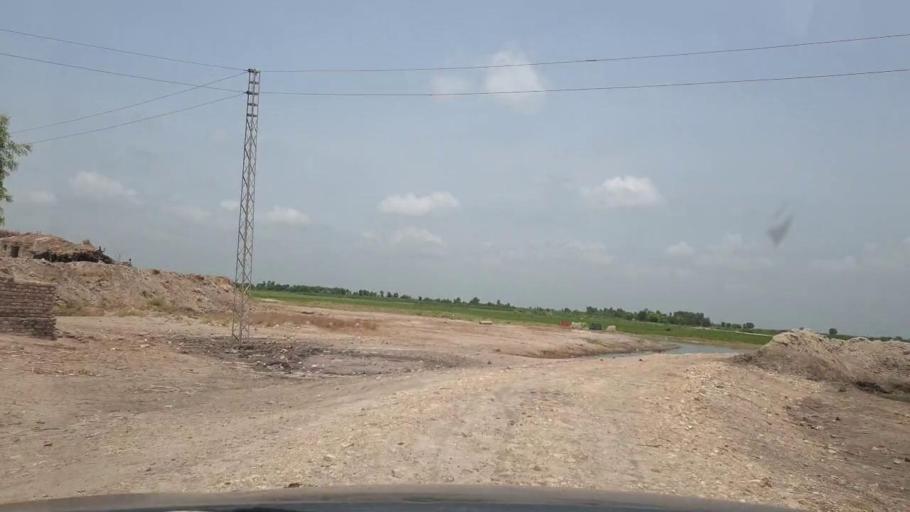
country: PK
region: Sindh
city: Ratodero
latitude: 27.9172
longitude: 68.3071
